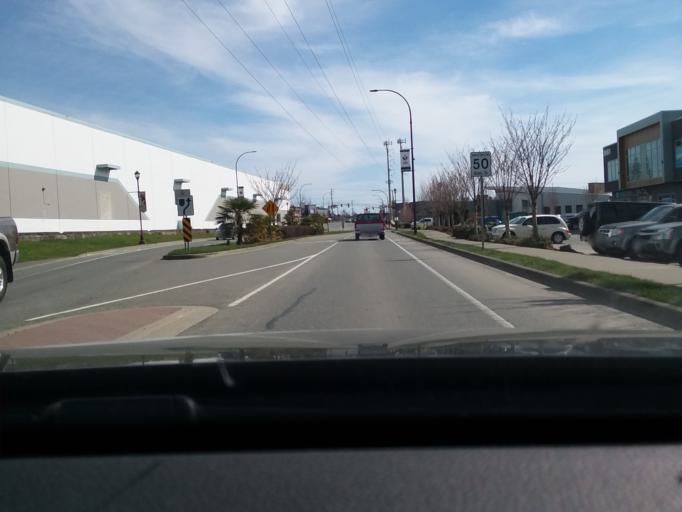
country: CA
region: British Columbia
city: Langford
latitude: 48.4429
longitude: -123.5137
